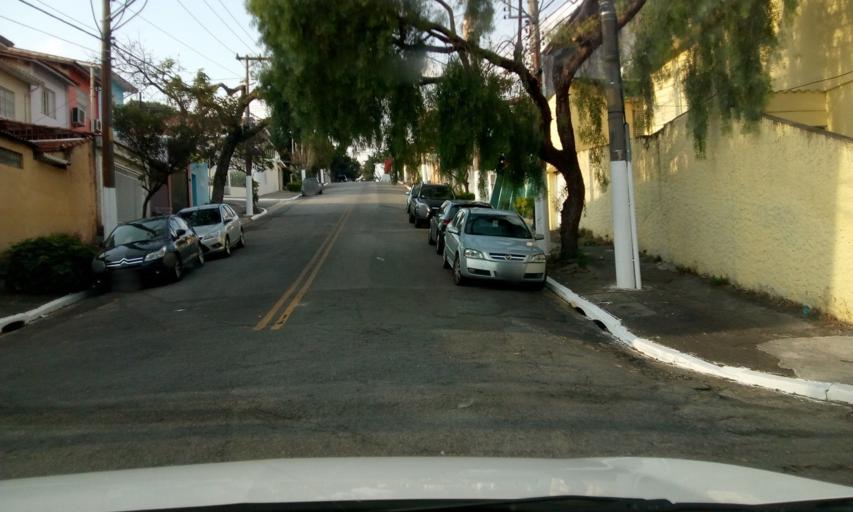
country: BR
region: Sao Paulo
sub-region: Diadema
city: Diadema
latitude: -23.6200
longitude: -46.6550
